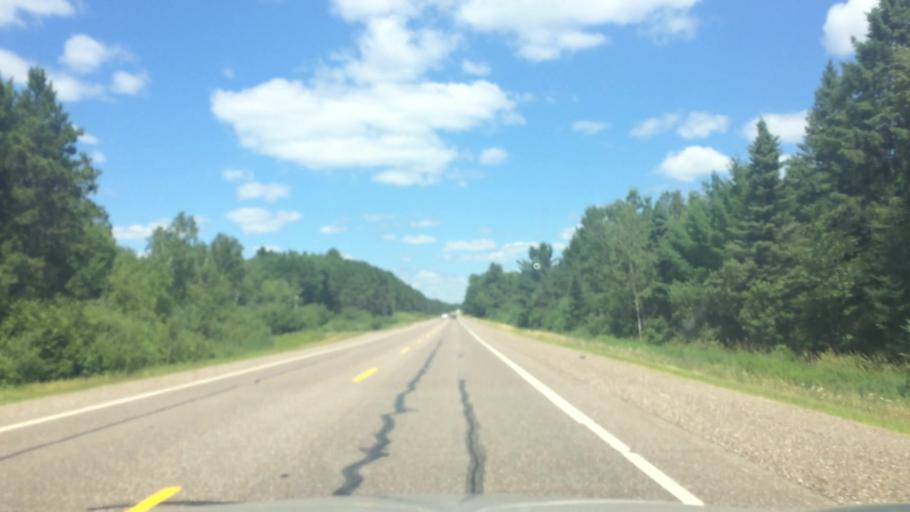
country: US
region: Wisconsin
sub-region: Vilas County
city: Lac du Flambeau
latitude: 45.9566
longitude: -89.7005
